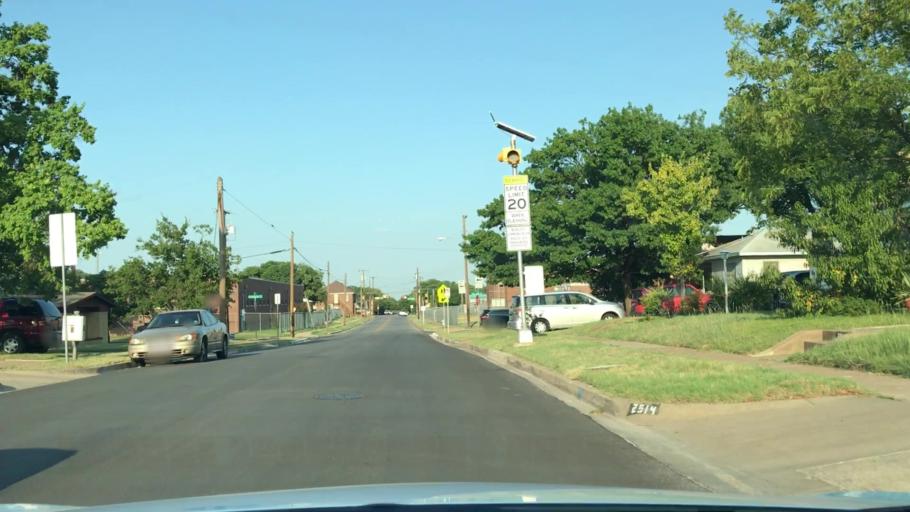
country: US
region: Texas
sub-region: Dallas County
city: Cockrell Hill
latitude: 32.7413
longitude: -96.8599
